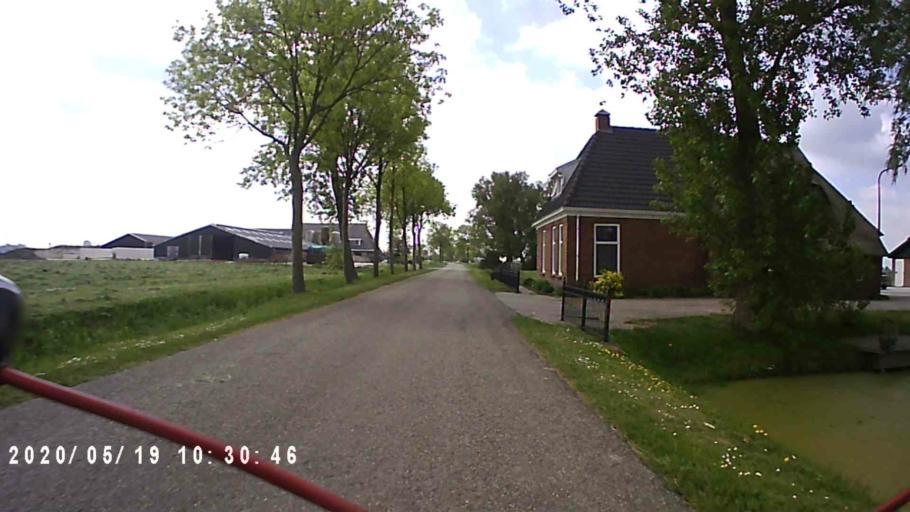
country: NL
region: Friesland
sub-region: Gemeente Kollumerland en Nieuwkruisland
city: Kollum
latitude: 53.2936
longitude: 6.1960
